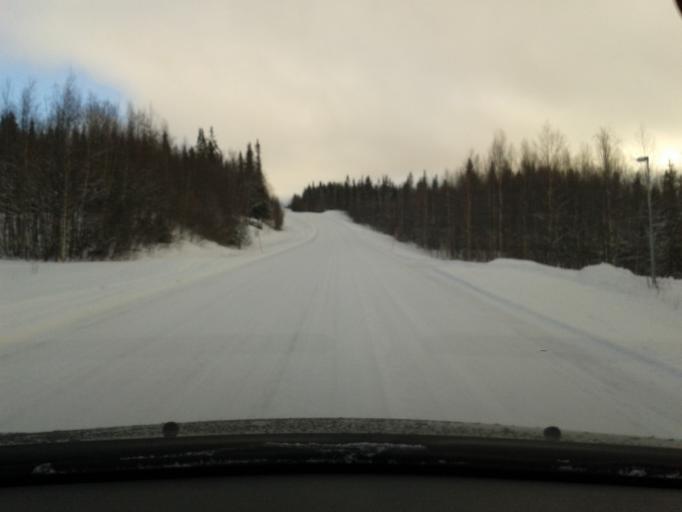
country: SE
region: Vaesterbotten
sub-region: Vilhelmina Kommun
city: Sjoberg
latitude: 65.2505
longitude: 15.5927
